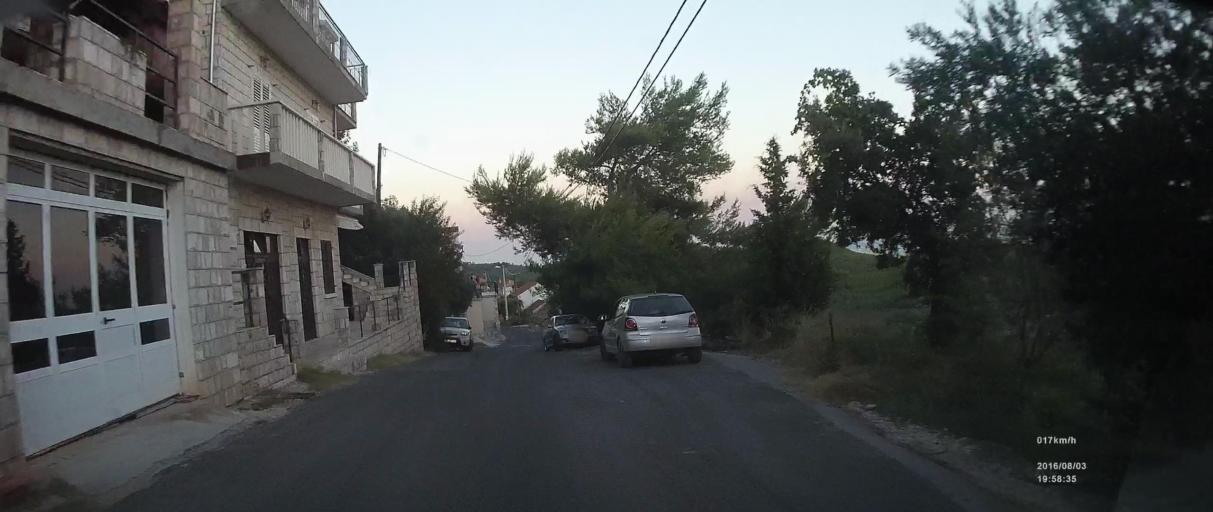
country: HR
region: Dubrovacko-Neretvanska
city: Blato
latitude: 42.7341
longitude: 17.5551
